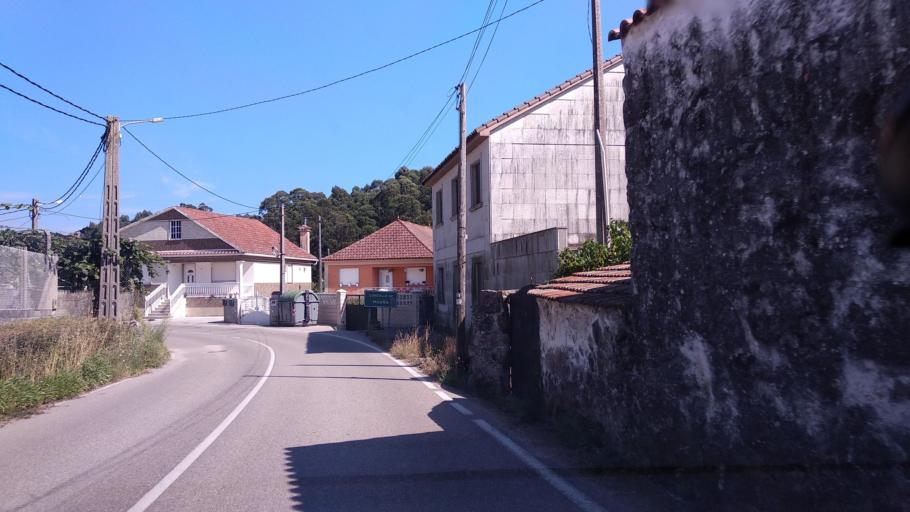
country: ES
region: Galicia
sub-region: Provincia de Pontevedra
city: Moana
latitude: 42.2758
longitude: -8.7614
